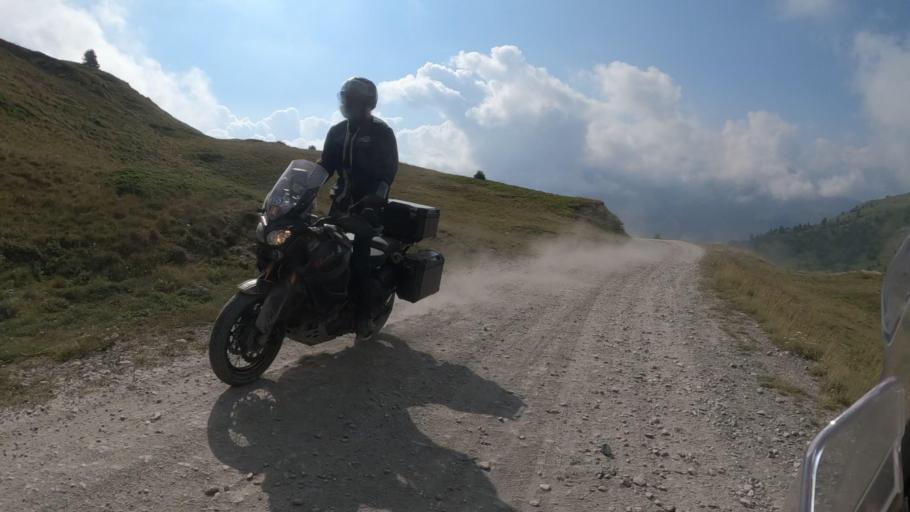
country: IT
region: Piedmont
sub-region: Provincia di Torino
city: Sestriere
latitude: 44.9811
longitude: 6.8729
